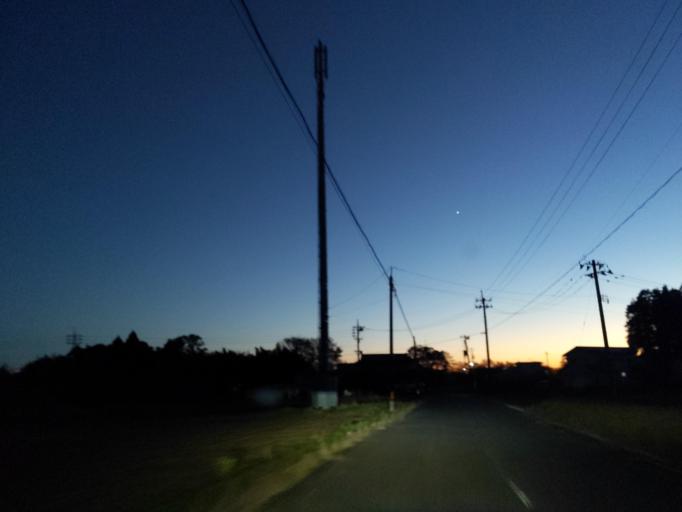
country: JP
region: Fukushima
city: Sukagawa
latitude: 37.3358
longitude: 140.3887
